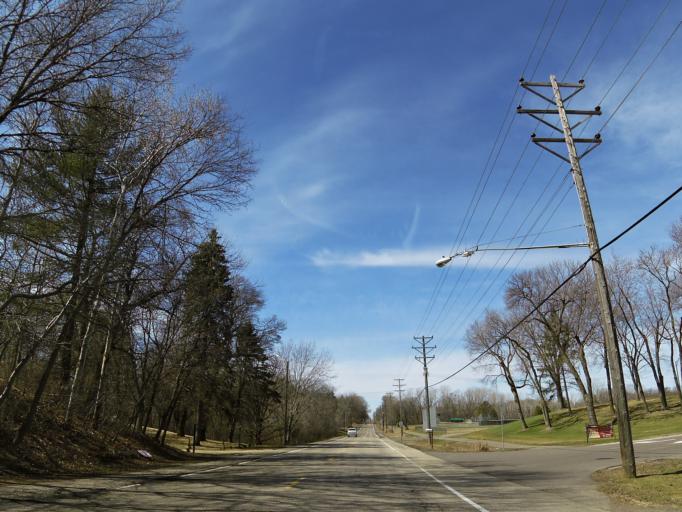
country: US
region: Minnesota
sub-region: Ramsey County
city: North Saint Paul
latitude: 44.9923
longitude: -92.9909
